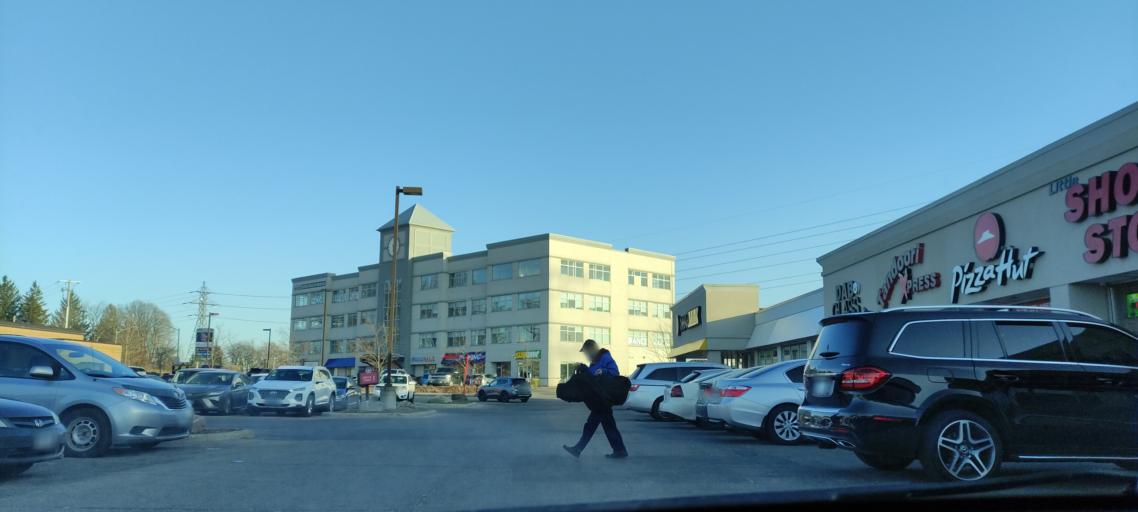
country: CA
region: Ontario
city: Kitchener
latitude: 43.4155
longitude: -80.5113
